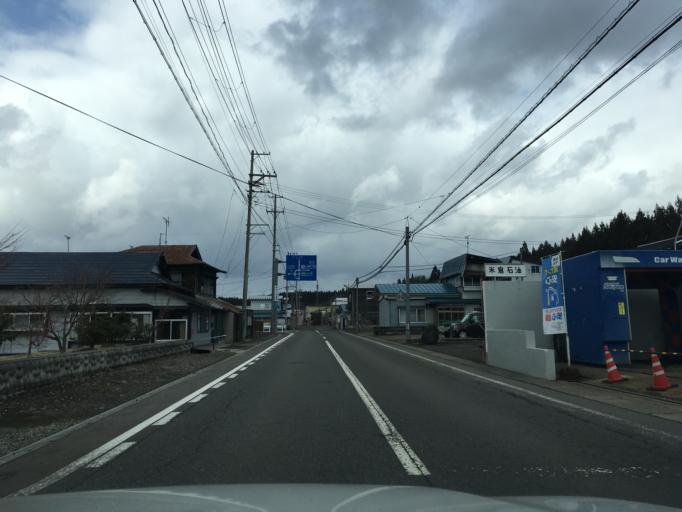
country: JP
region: Akita
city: Takanosu
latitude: 40.1572
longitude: 140.3338
